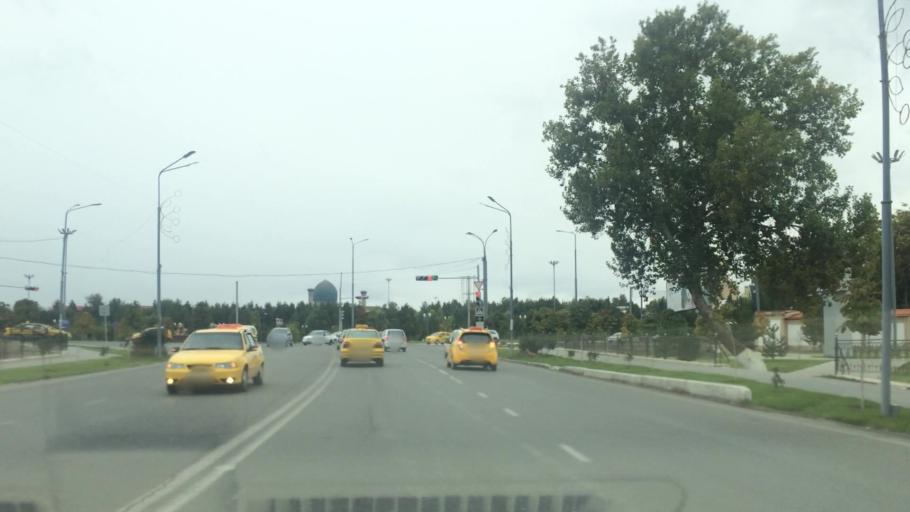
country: UZ
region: Samarqand
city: Samarqand
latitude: 39.6531
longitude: 66.9701
